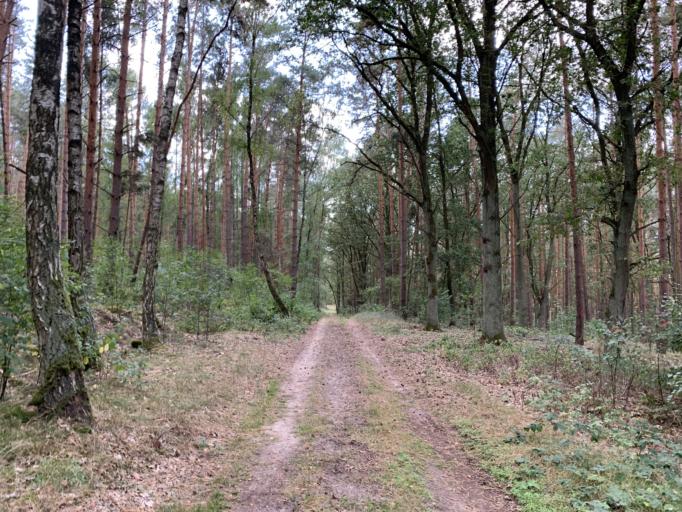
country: DE
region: Brandenburg
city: Michendorf
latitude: 52.3162
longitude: 12.9888
